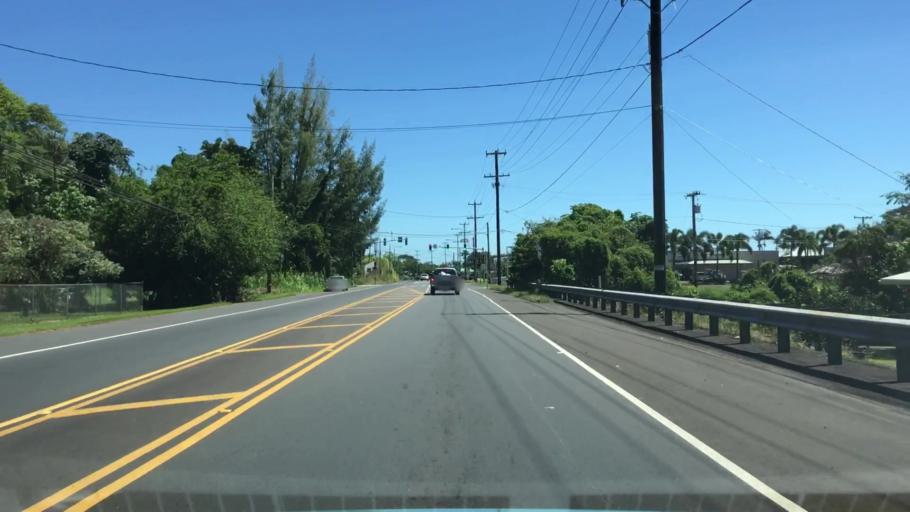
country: US
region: Hawaii
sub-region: Hawaii County
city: Kurtistown
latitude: 19.5921
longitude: -155.0588
